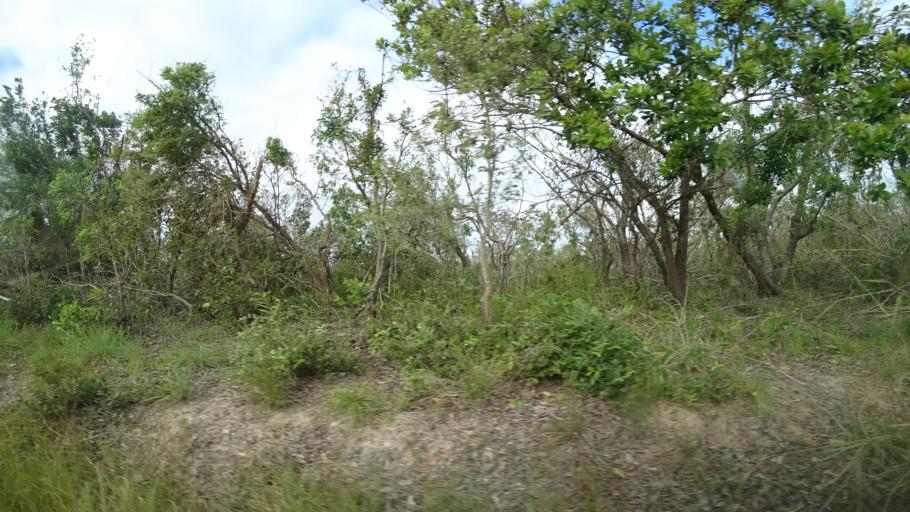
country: MZ
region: Sofala
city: Beira
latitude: -19.6479
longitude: 35.0587
